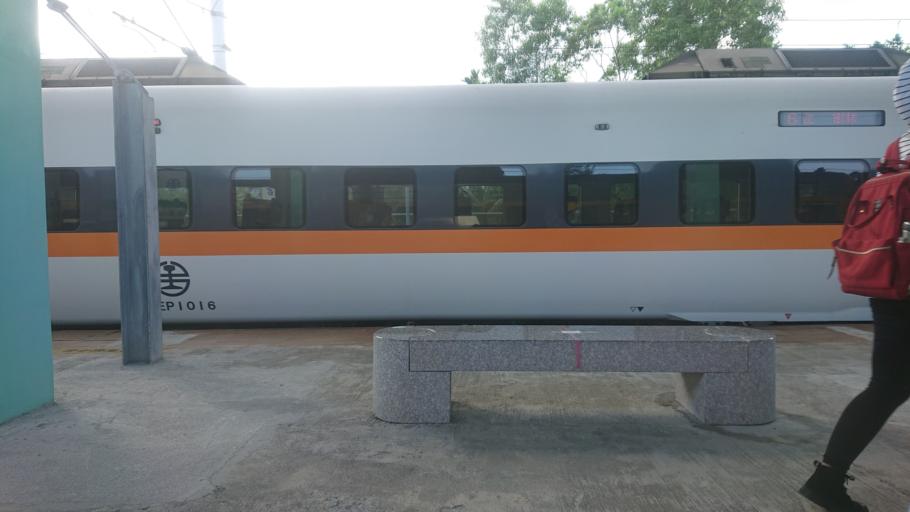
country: TW
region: Taiwan
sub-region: Hualien
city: Hualian
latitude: 23.9671
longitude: 121.5817
